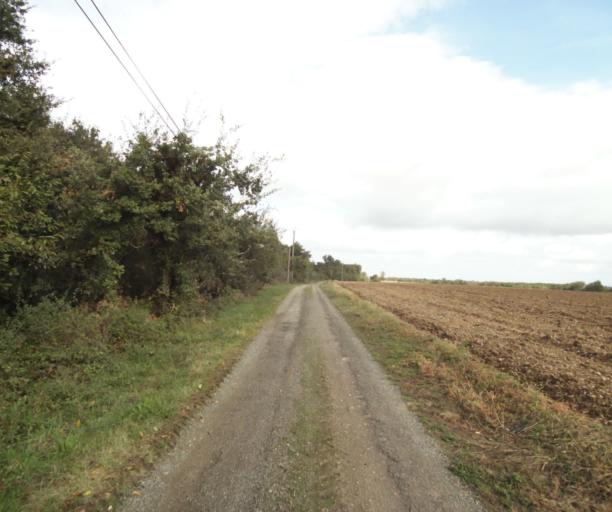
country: FR
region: Midi-Pyrenees
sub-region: Departement du Tarn-et-Garonne
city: Beaumont-de-Lomagne
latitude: 43.8794
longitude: 1.0723
